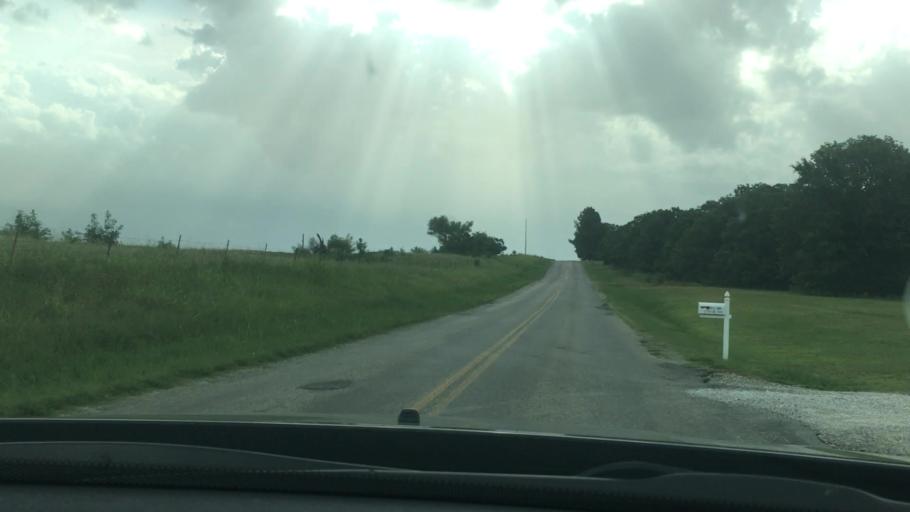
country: US
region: Oklahoma
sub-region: Pontotoc County
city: Ada
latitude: 34.8106
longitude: -96.6392
